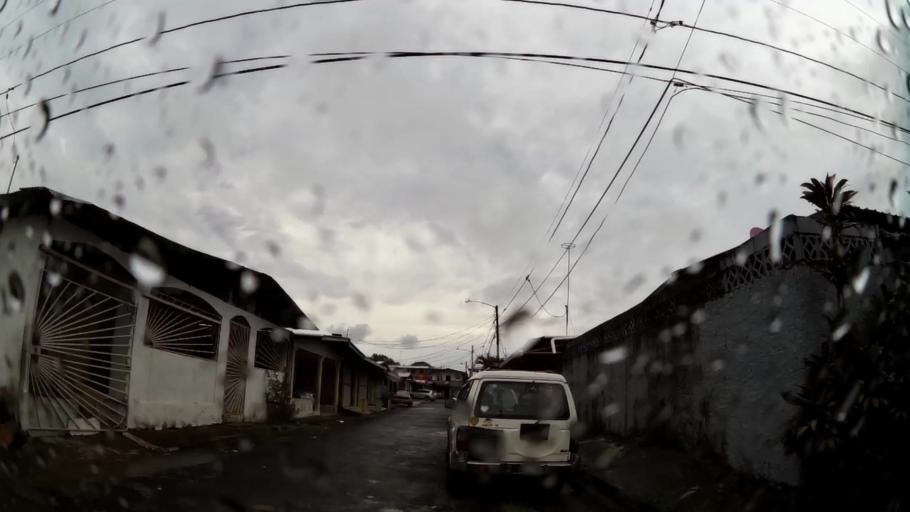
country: PA
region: Colon
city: Las Margaritas
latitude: 9.3324
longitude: -79.8738
